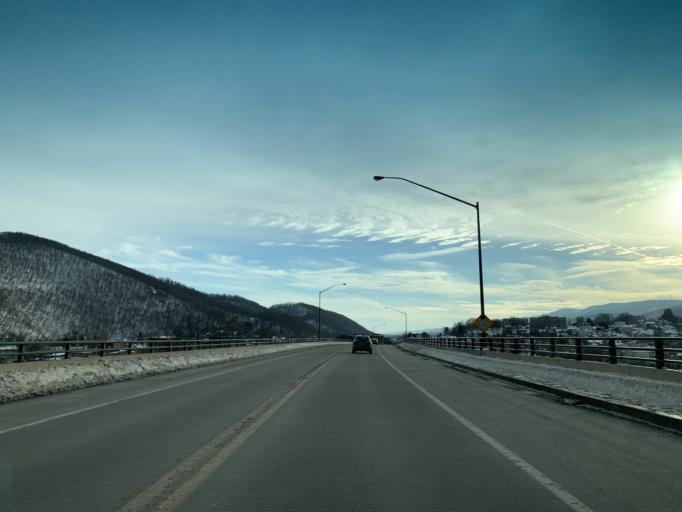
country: US
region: West Virginia
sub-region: Mineral County
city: Keyser
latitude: 39.4438
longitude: -78.9736
